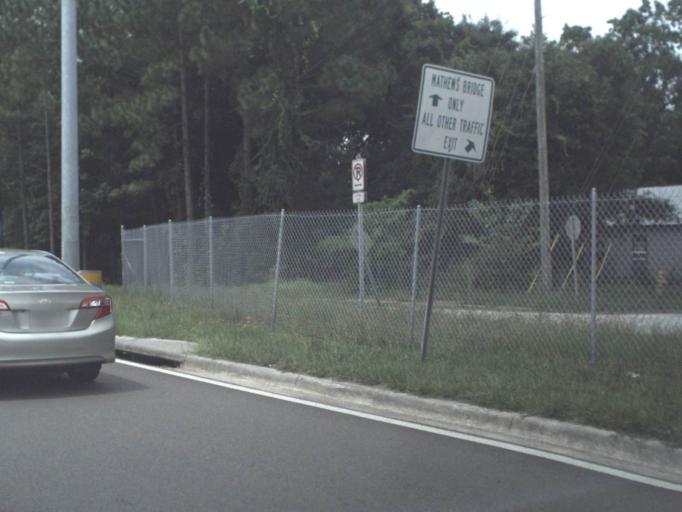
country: US
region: Florida
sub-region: Duval County
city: Jacksonville
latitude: 30.3299
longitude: -81.6367
